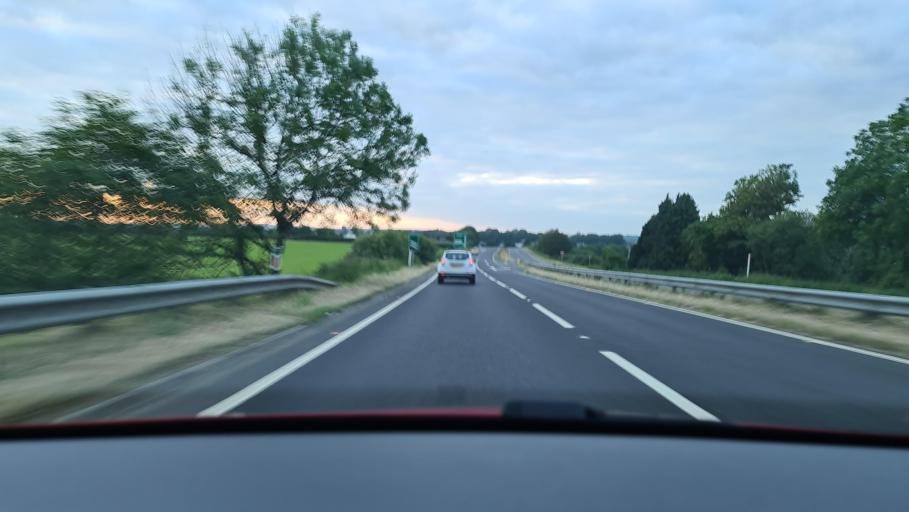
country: GB
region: England
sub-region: Cornwall
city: Liskeard
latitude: 50.4441
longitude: -4.4464
